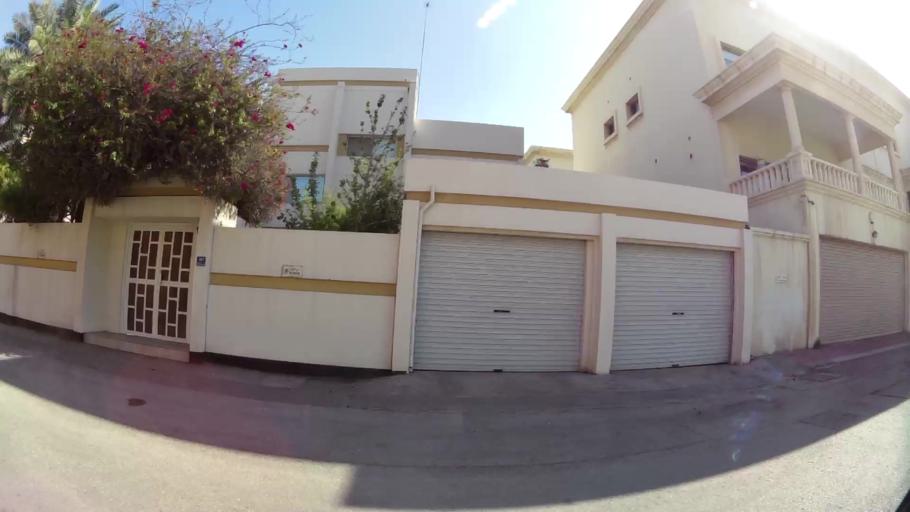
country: BH
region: Manama
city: Manama
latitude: 26.2110
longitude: 50.5895
